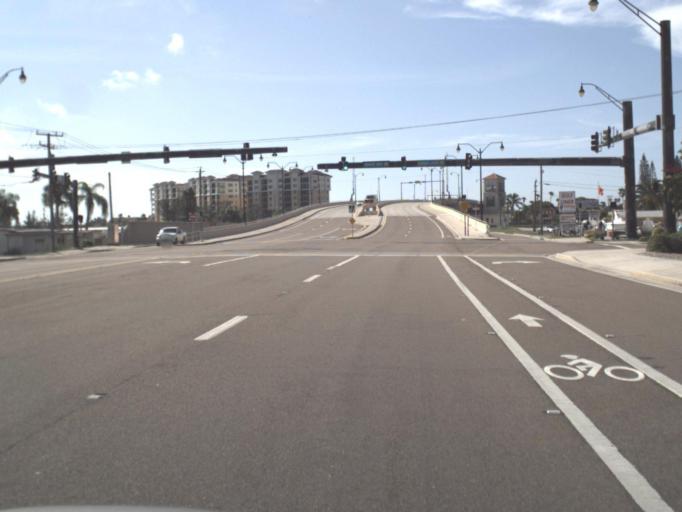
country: US
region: Florida
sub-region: Sarasota County
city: Venice
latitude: 27.1066
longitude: -82.4442
